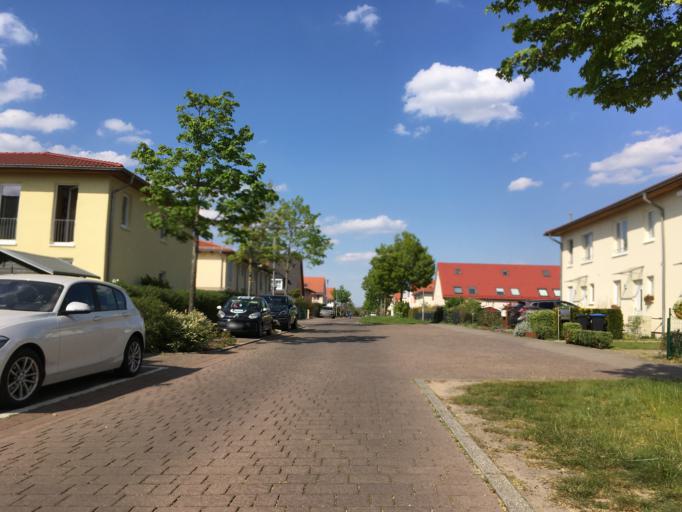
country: DE
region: Berlin
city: Falkenberg
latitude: 52.5707
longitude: 13.5543
